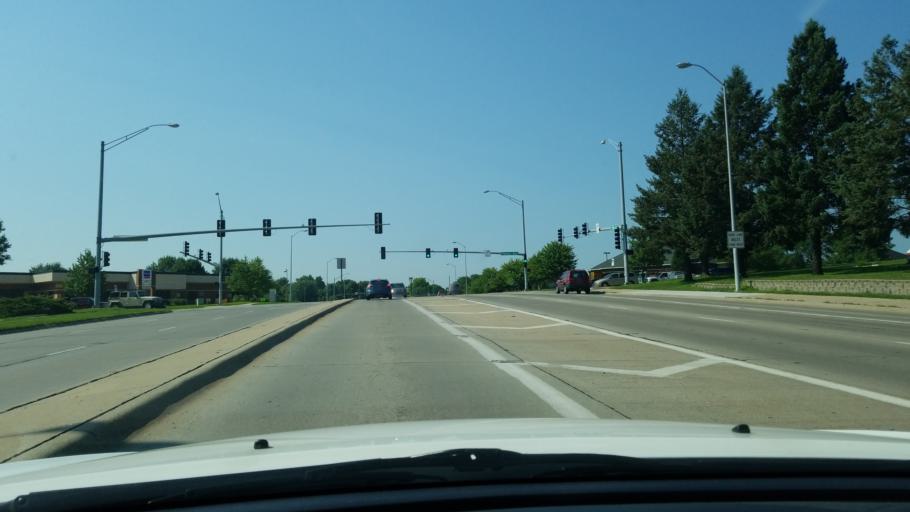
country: US
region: Nebraska
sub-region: Lancaster County
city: Lincoln
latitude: 40.7704
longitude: -96.6252
